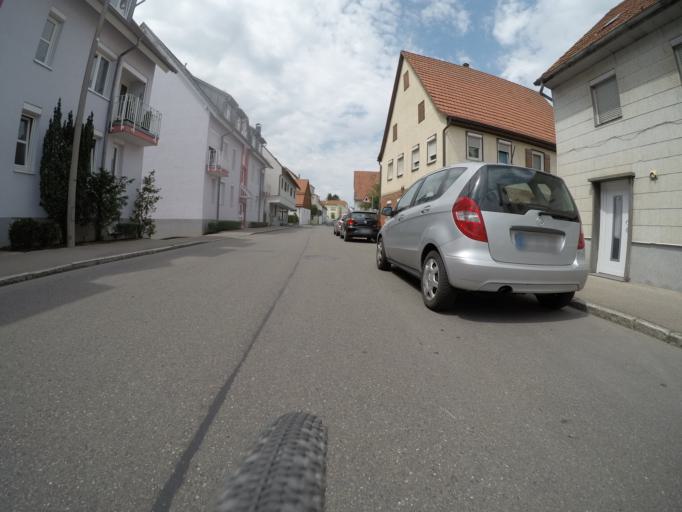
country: DE
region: Baden-Wuerttemberg
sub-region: Regierungsbezirk Stuttgart
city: Magstadt
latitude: 48.7254
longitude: 8.9641
